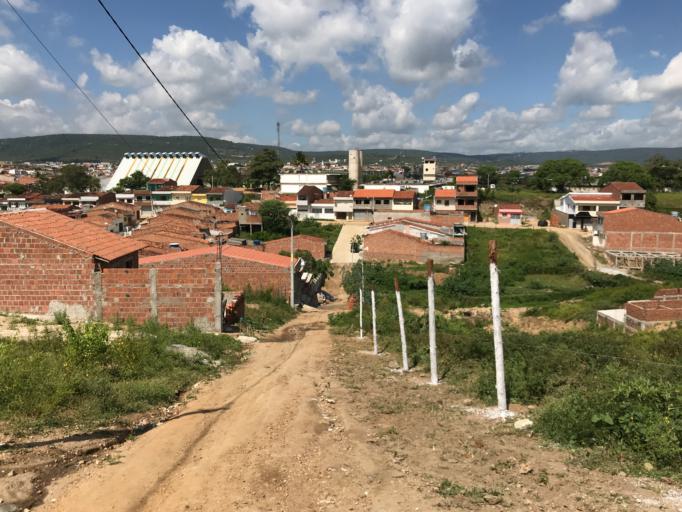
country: BR
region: Pernambuco
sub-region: Bezerros
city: Bezerros
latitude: -8.2288
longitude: -35.7569
